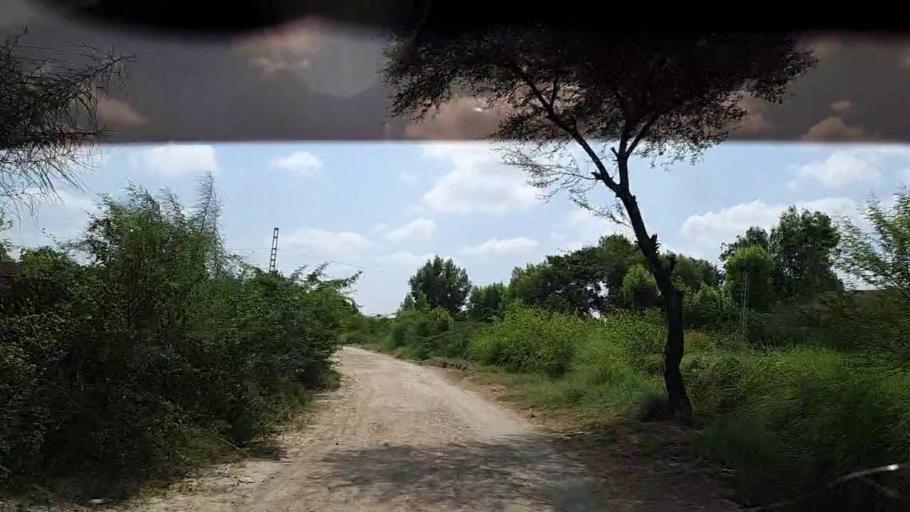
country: PK
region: Sindh
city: Kadhan
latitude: 24.5913
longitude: 68.9579
